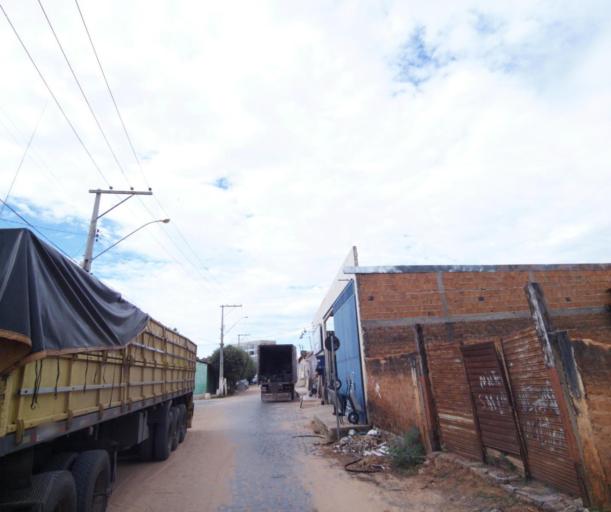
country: BR
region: Bahia
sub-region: Carinhanha
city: Carinhanha
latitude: -14.1767
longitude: -44.5311
